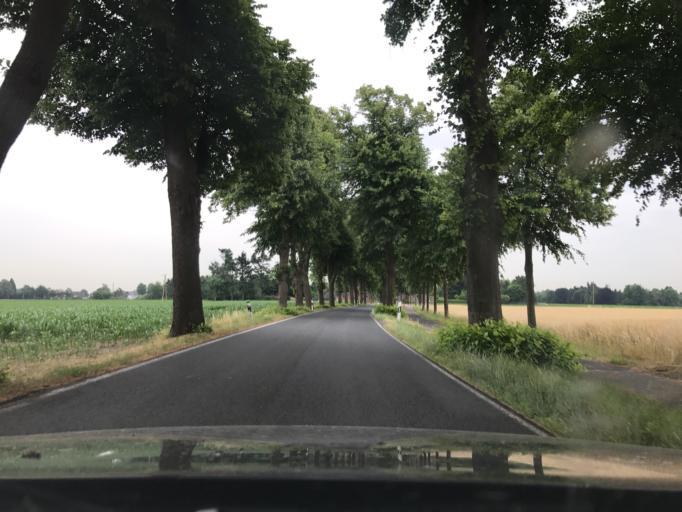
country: DE
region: North Rhine-Westphalia
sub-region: Regierungsbezirk Dusseldorf
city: Grefrath
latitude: 51.3520
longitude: 6.3647
